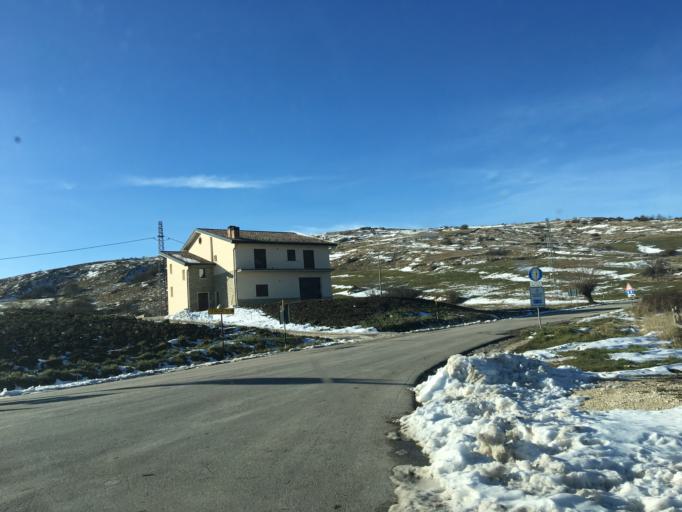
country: IT
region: Abruzzo
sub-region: Provincia di Chieti
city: Rosello
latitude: 41.8564
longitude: 14.3572
